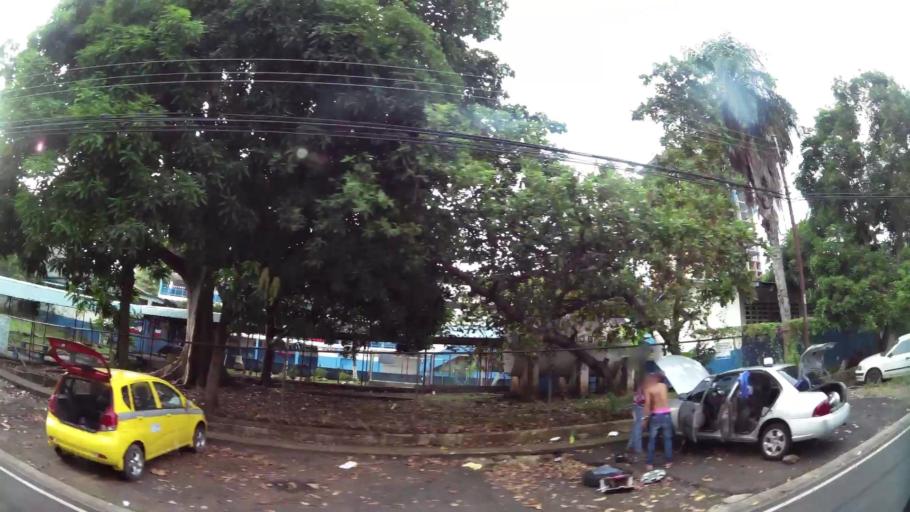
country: PA
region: Panama
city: Panama
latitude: 8.9985
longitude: -79.5141
